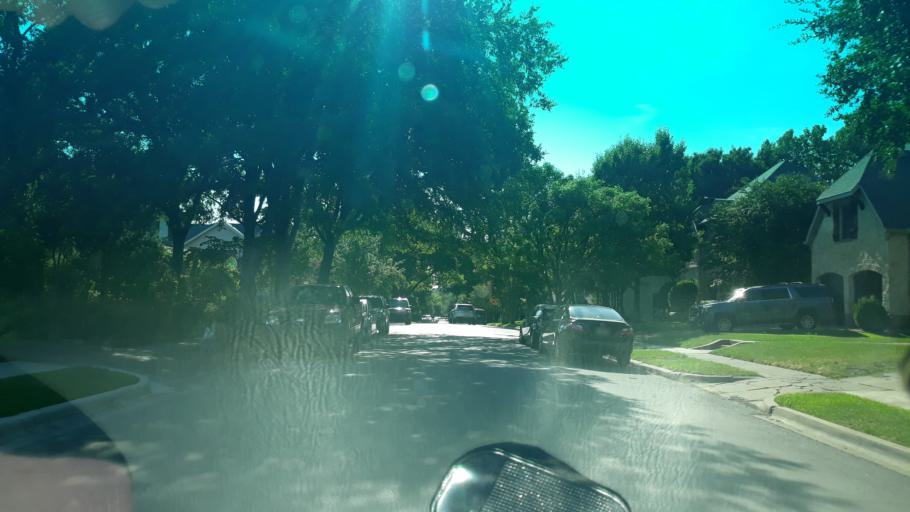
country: US
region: Texas
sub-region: Dallas County
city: Highland Park
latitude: 32.8231
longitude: -96.7564
